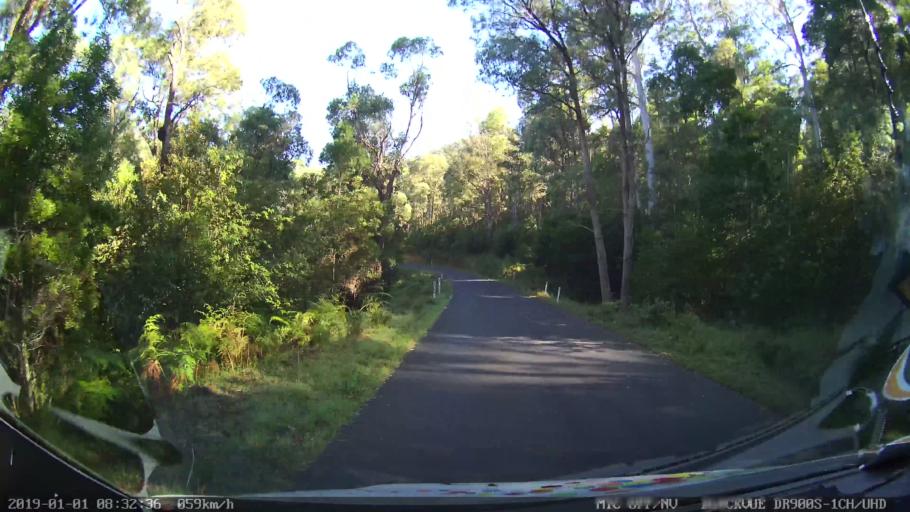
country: AU
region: New South Wales
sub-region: Snowy River
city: Jindabyne
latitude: -36.3605
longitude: 148.2063
